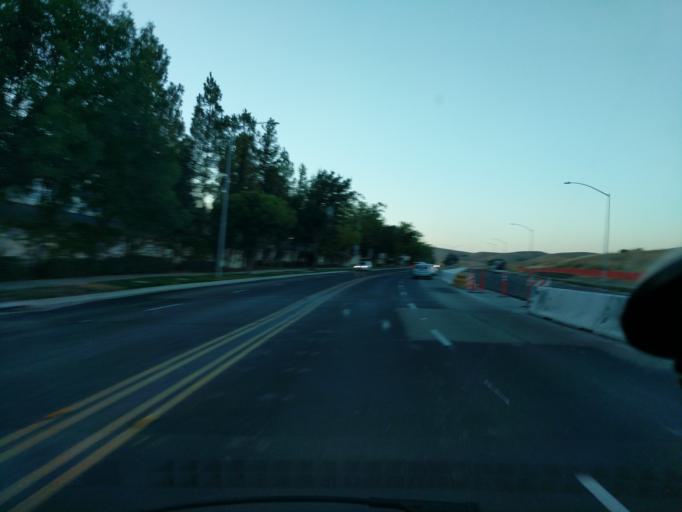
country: US
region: California
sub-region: Alameda County
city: Dublin
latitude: 37.7288
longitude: -121.9107
